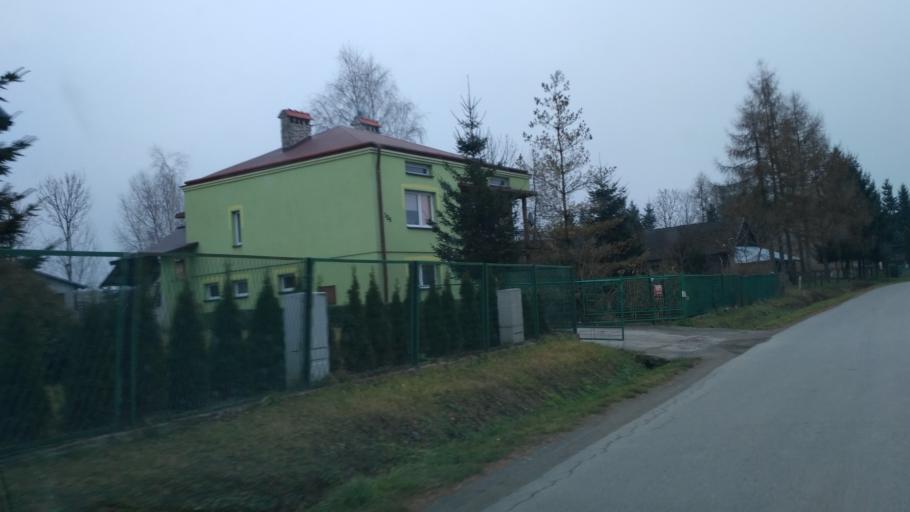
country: PL
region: Subcarpathian Voivodeship
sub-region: Powiat jaroslawski
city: Pawlosiow
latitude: 49.9651
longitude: 22.6494
